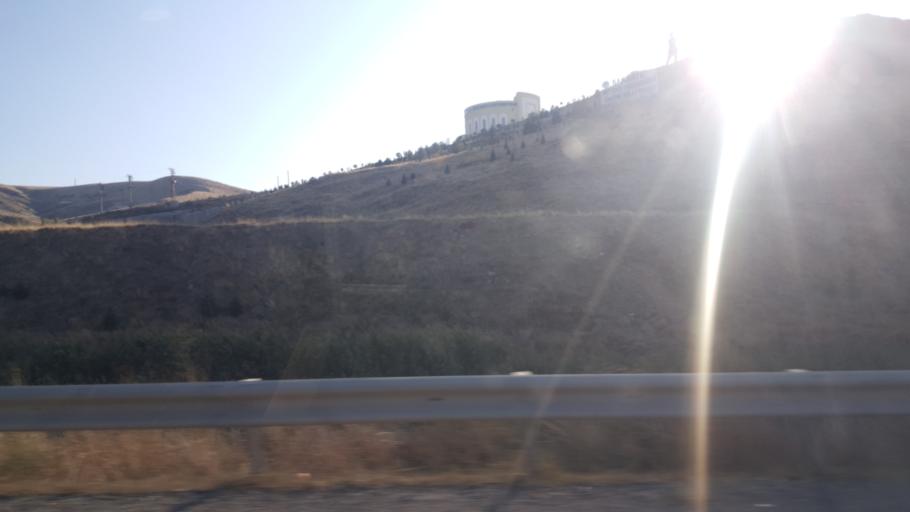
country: TR
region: Ankara
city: Polatli
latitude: 39.5775
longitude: 32.0641
